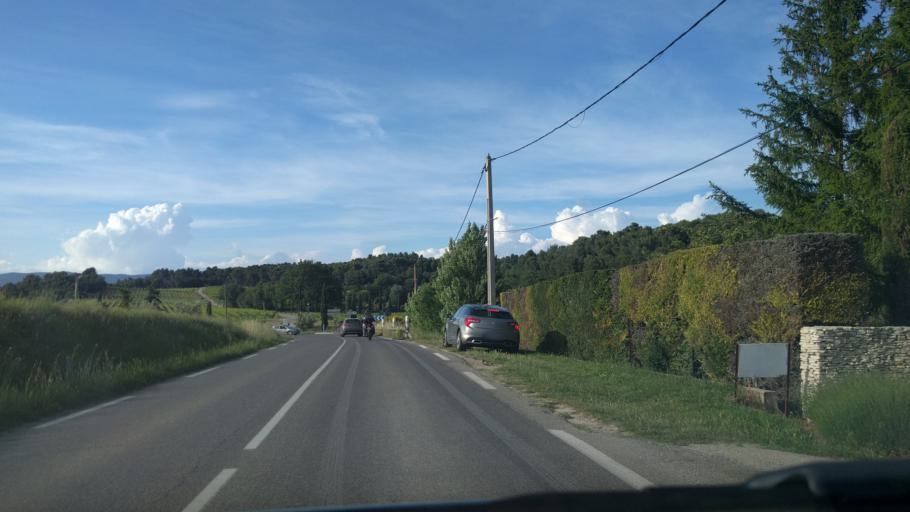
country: FR
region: Provence-Alpes-Cote d'Azur
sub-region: Departement du Vaucluse
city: Pertuis
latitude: 43.7347
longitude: 5.5110
